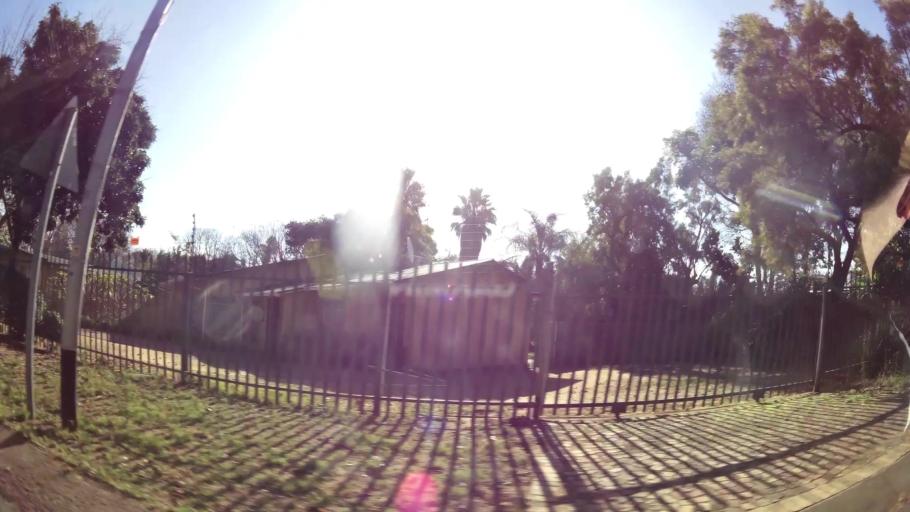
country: ZA
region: Gauteng
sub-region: City of Tshwane Metropolitan Municipality
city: Pretoria
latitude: -25.7296
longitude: 28.2684
